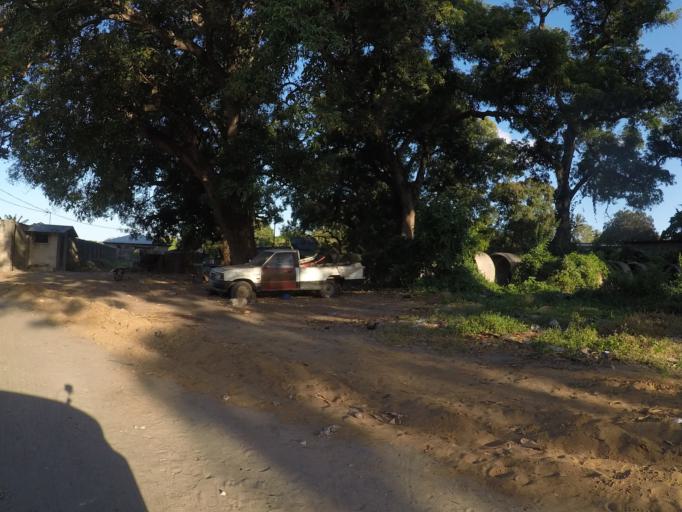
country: TZ
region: Zanzibar Urban/West
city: Zanzibar
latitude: -6.1713
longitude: 39.1999
